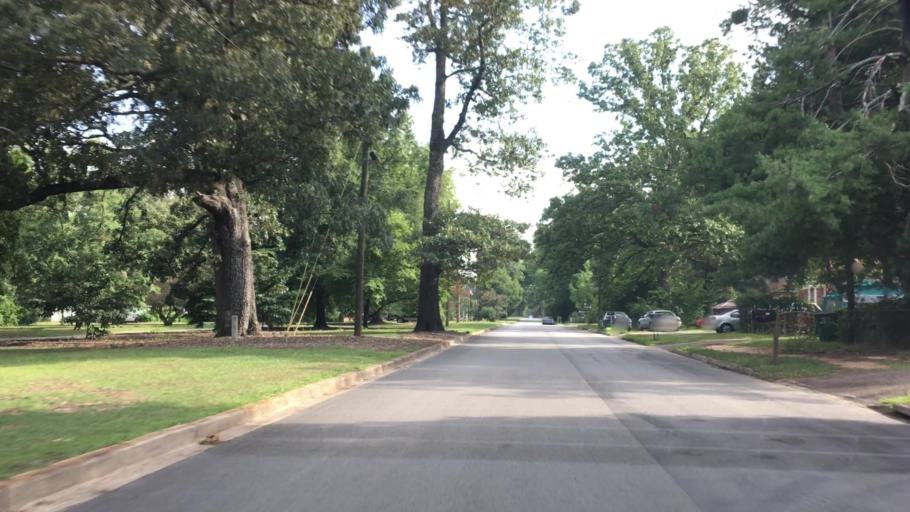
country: US
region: South Carolina
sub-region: Aiken County
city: Aiken
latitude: 33.5674
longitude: -81.7162
